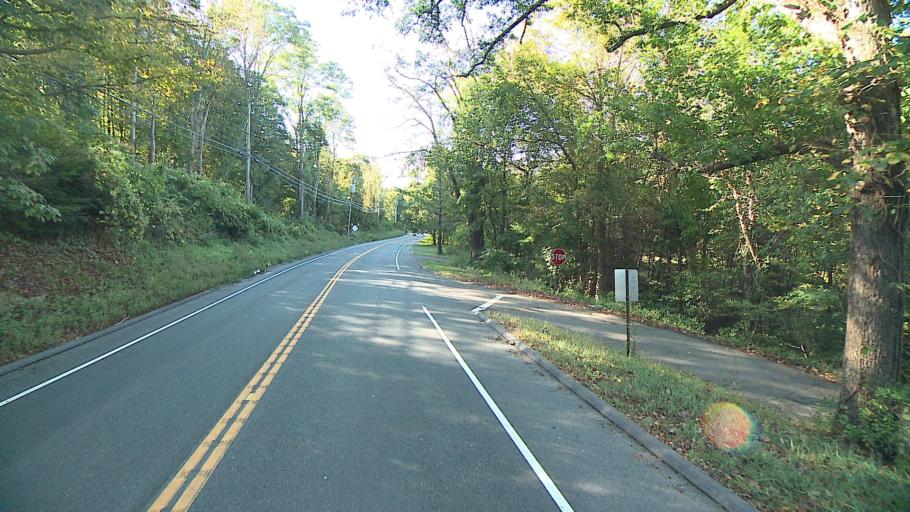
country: US
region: Connecticut
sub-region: Litchfield County
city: New Milford
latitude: 41.6187
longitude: -73.3977
